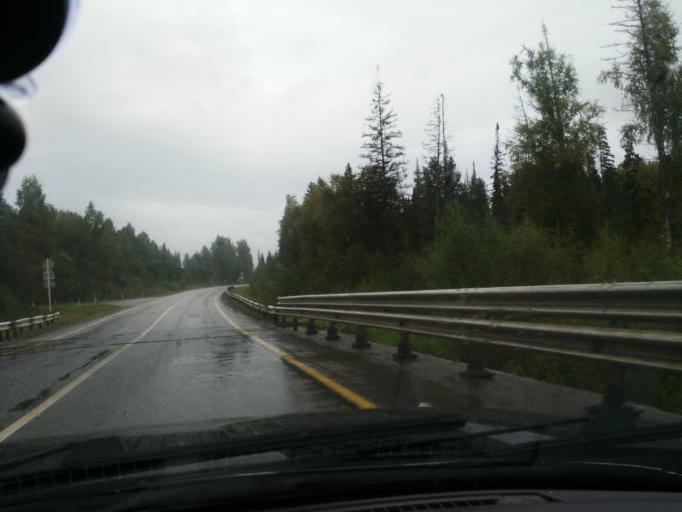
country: RU
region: Perm
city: Osa
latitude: 57.3882
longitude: 55.6086
